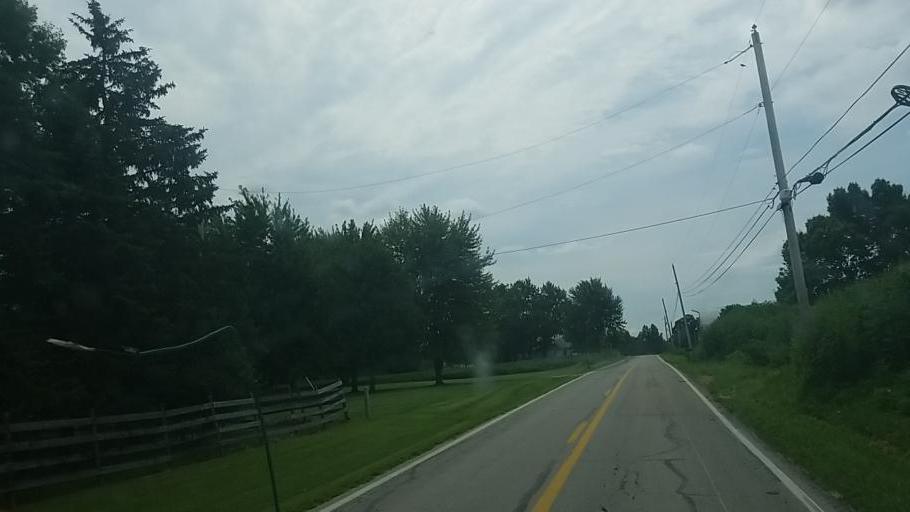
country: US
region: Ohio
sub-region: Franklin County
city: New Albany
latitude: 40.1376
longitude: -82.8216
